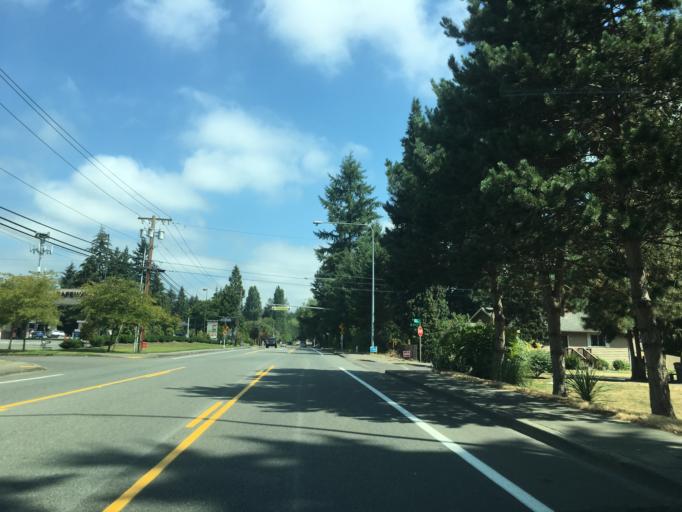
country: US
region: Washington
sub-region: King County
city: Inglewood-Finn Hill
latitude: 47.7221
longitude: -122.2057
